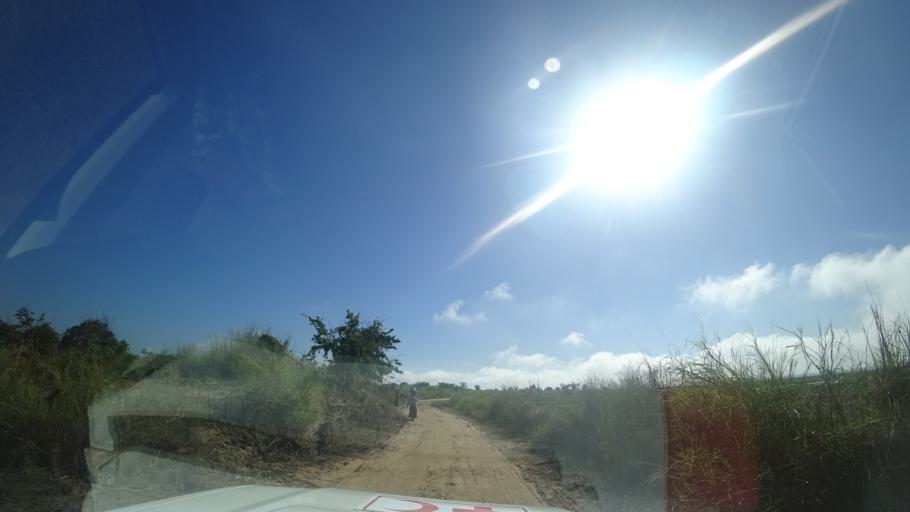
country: MZ
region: Sofala
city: Dondo
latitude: -19.4263
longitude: 34.5615
